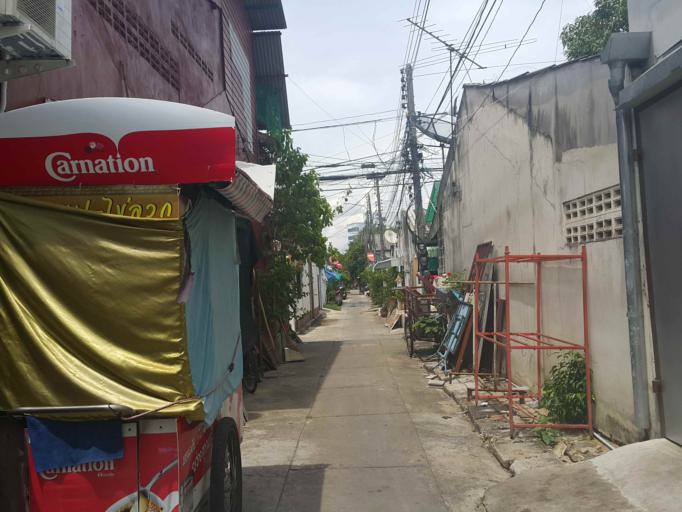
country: TH
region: Chiang Mai
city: Chiang Mai
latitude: 18.7610
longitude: 99.0120
